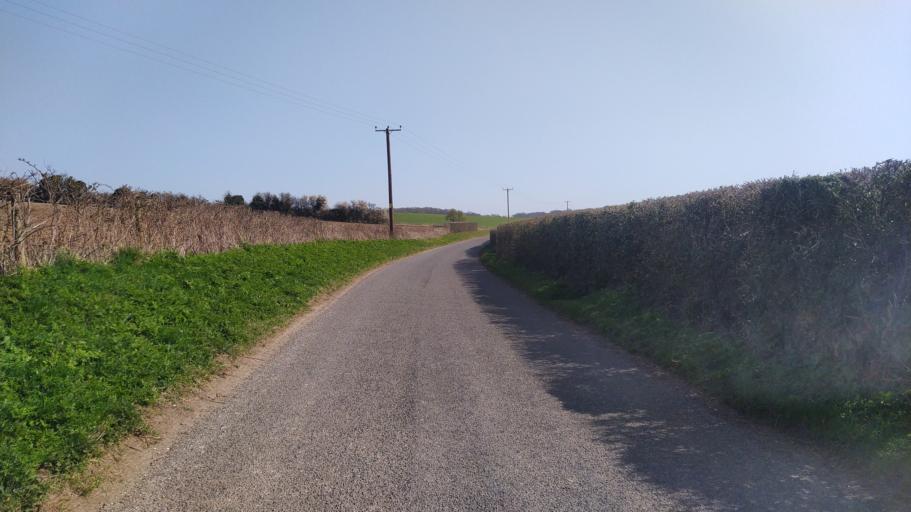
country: GB
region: England
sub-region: Hampshire
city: Kings Worthy
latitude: 51.0777
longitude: -1.2429
